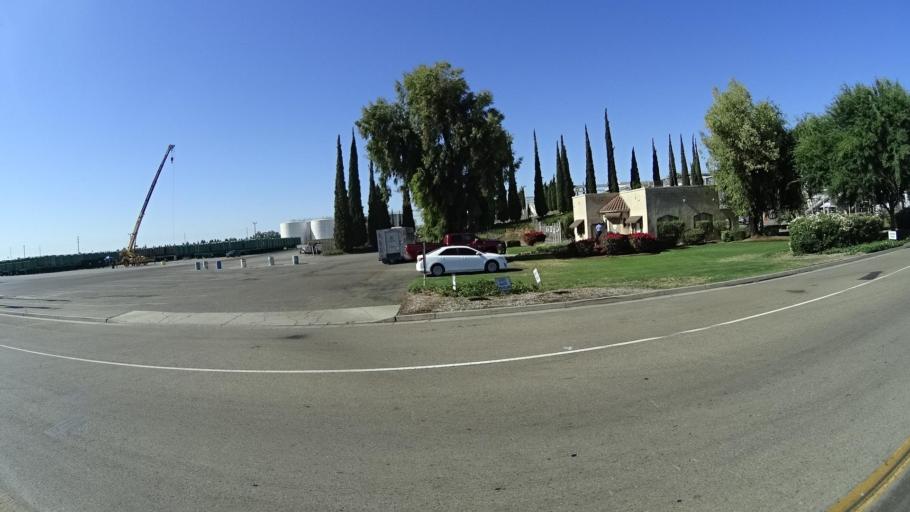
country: US
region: California
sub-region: Fresno County
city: Sunnyside
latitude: 36.7575
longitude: -119.6959
